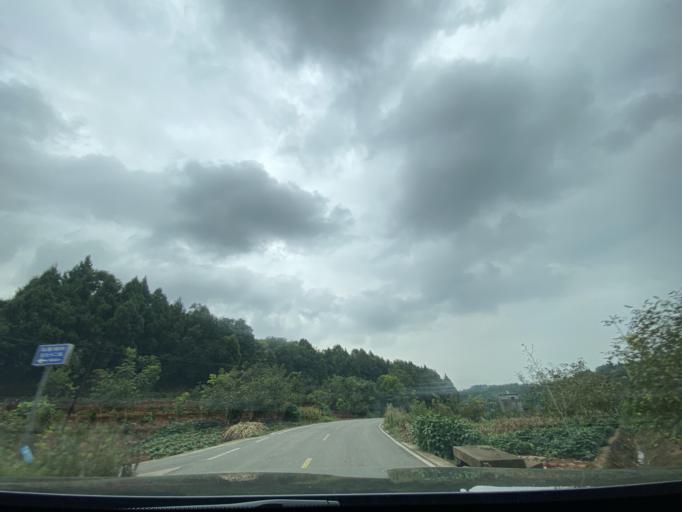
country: CN
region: Sichuan
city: Jiancheng
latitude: 30.5364
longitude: 104.5289
